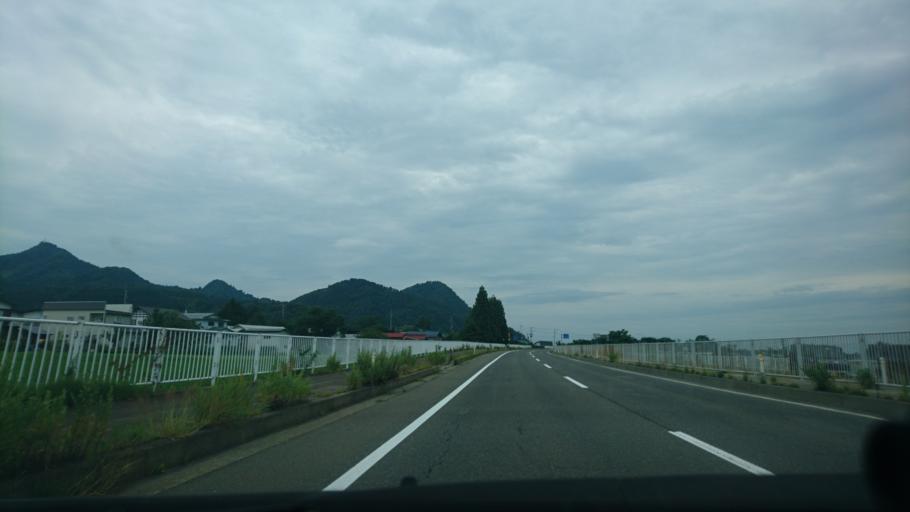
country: JP
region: Akita
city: Omagari
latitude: 39.4778
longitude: 140.4615
